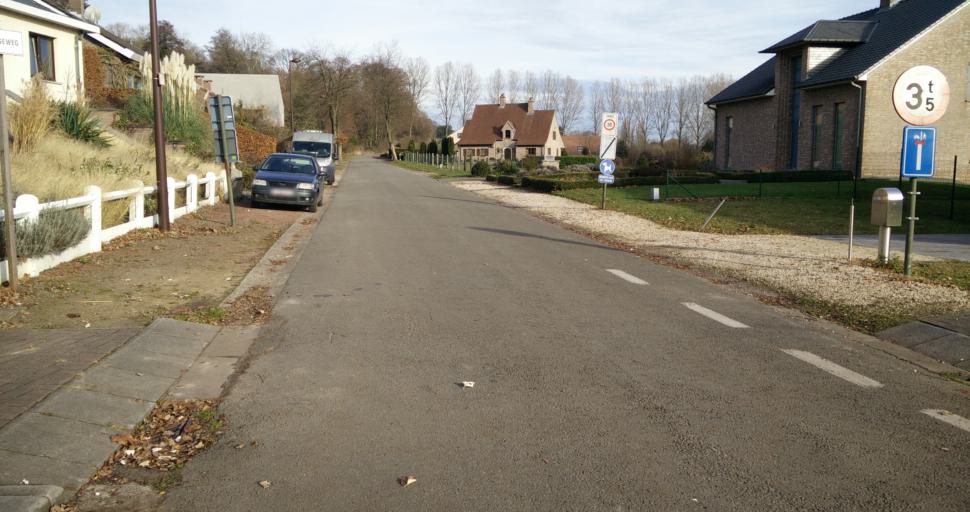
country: BE
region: Flanders
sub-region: Provincie Vlaams-Brabant
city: Linkebeek
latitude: 50.7355
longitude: 4.3203
